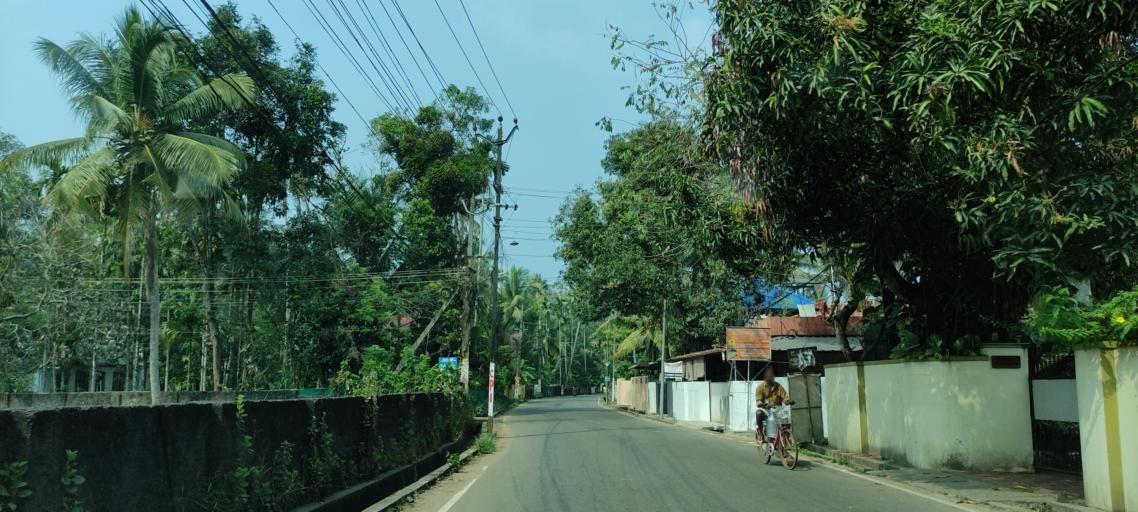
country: IN
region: Kerala
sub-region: Kottayam
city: Vaikam
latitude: 9.7518
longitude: 76.4024
